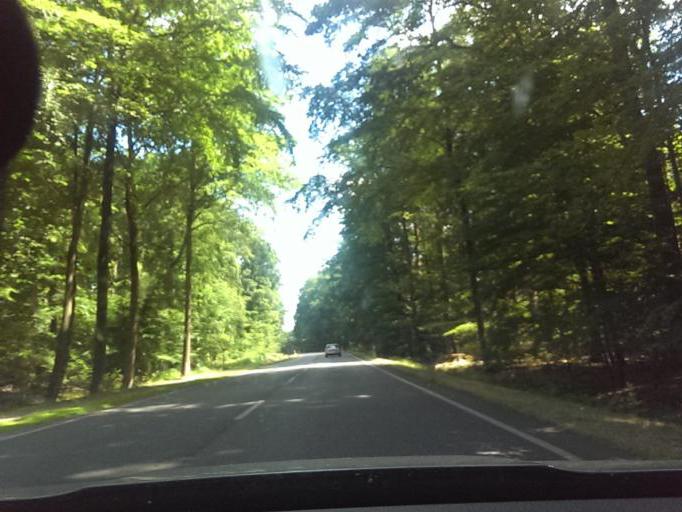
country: DE
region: Lower Saxony
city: Ahausen
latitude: 53.0345
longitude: 9.3053
